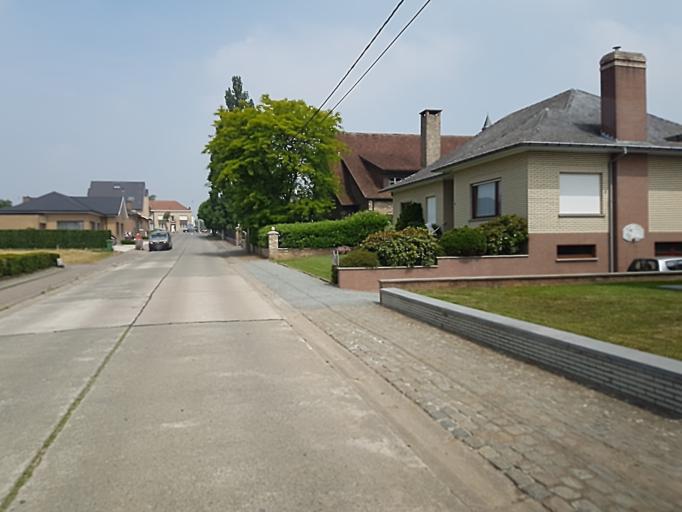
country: BE
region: Flanders
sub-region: Provincie Oost-Vlaanderen
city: Sint-Maria-Lierde
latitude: 50.8196
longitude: 3.8916
